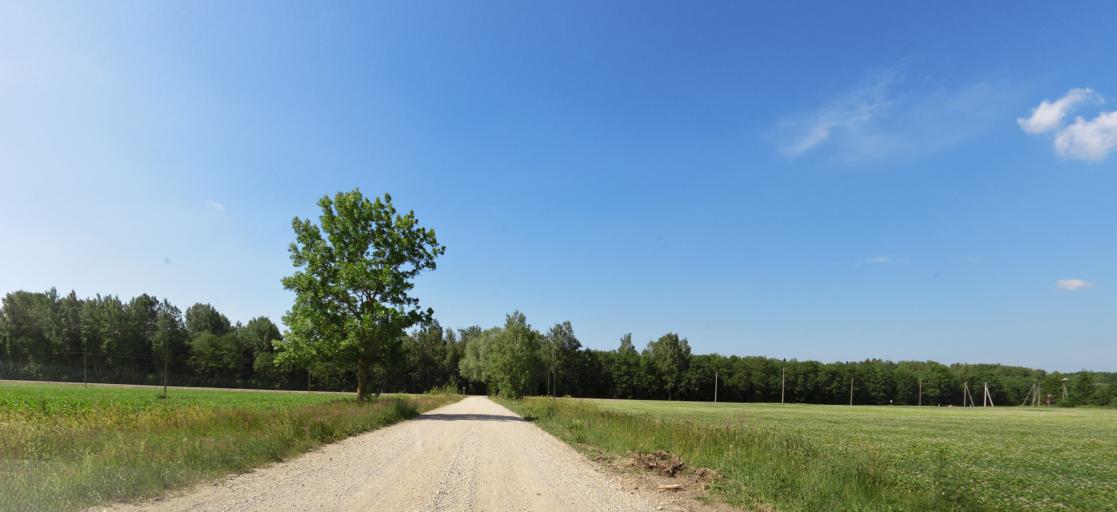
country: LT
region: Panevezys
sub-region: Birzai
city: Birzai
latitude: 56.2108
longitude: 24.9113
